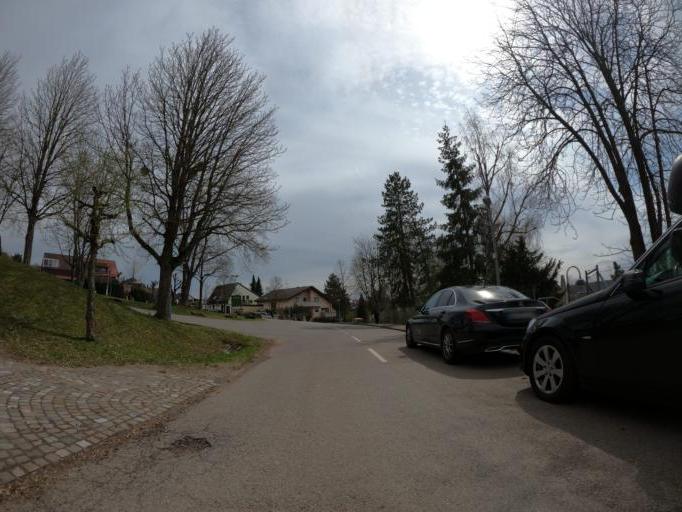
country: DE
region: Baden-Wuerttemberg
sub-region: Regierungsbezirk Stuttgart
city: Waldenbuch
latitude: 48.6460
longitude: 9.1383
